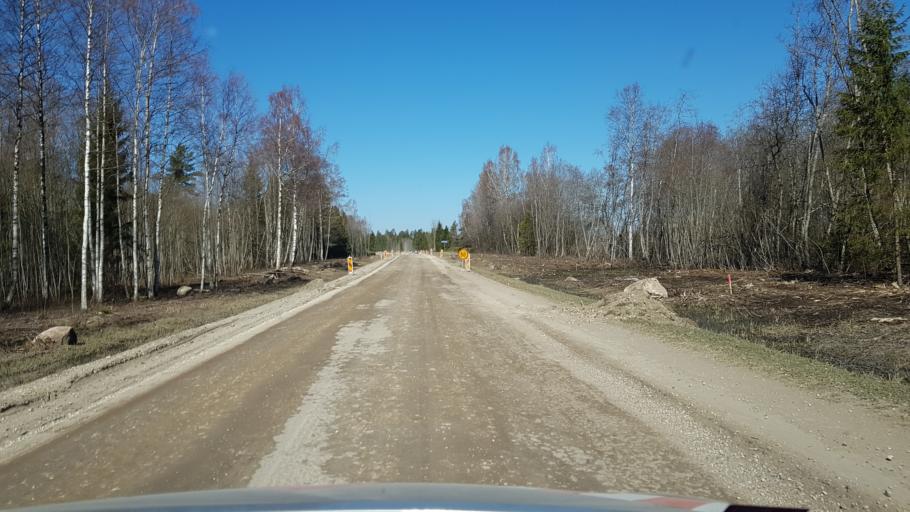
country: EE
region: Laeaene-Virumaa
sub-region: Vinni vald
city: Vinni
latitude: 59.0540
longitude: 26.6521
